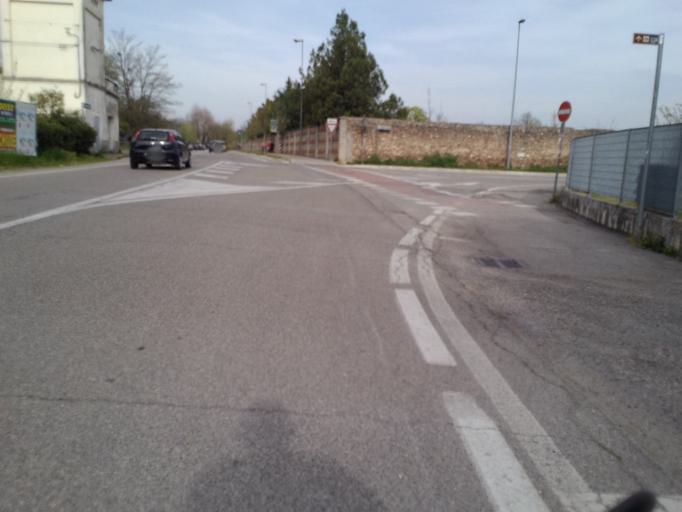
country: IT
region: Veneto
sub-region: Provincia di Verona
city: Villafranca di Verona
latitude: 45.3491
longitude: 10.8403
